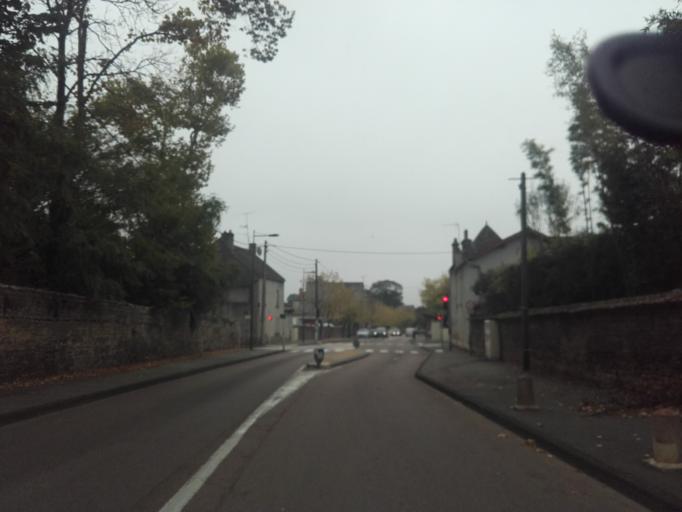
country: FR
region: Bourgogne
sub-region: Departement de la Cote-d'Or
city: Beaune
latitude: 47.0252
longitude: 4.8266
